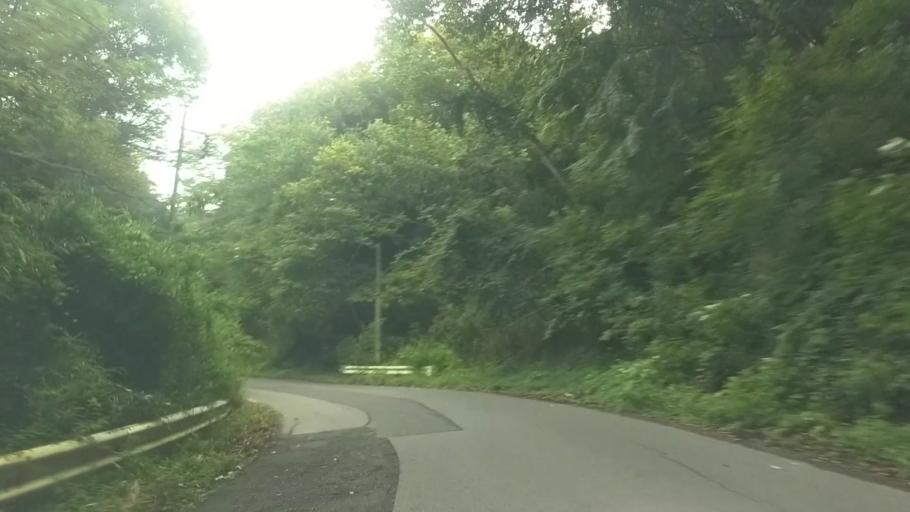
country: JP
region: Chiba
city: Kawaguchi
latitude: 35.2261
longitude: 140.0268
